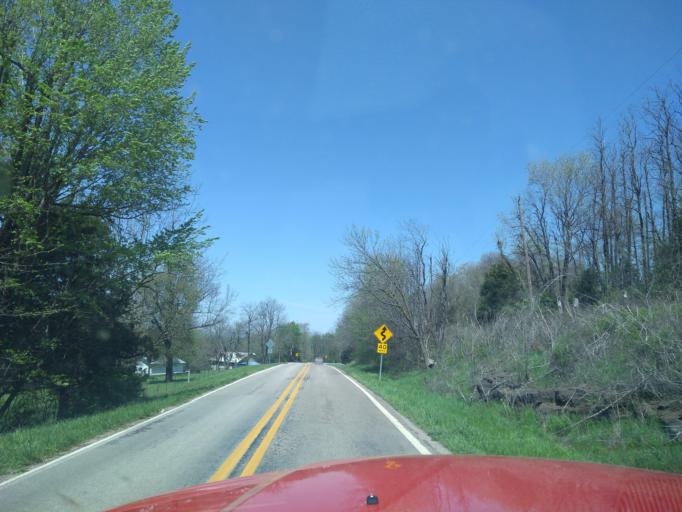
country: US
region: Arkansas
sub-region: Washington County
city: West Fork
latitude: 35.8917
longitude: -94.2431
